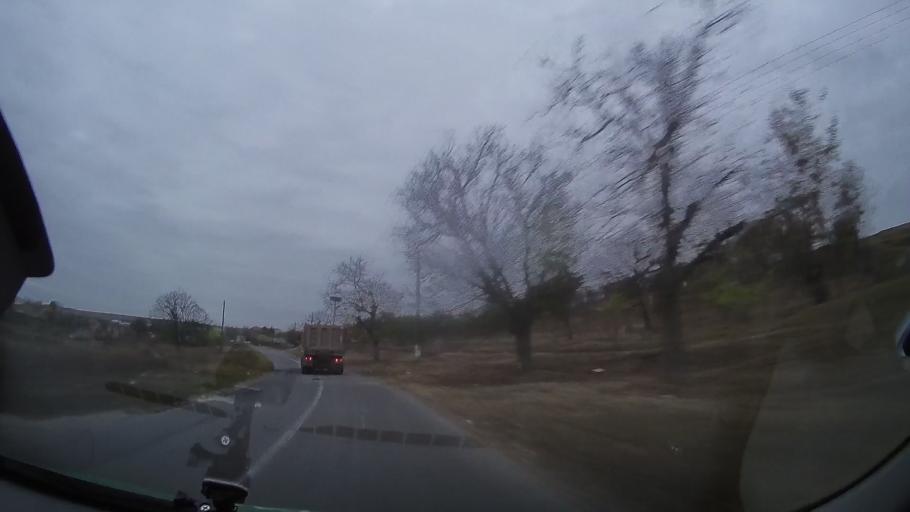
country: RO
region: Tulcea
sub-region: Comuna Mihai Bravu
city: Mihai Bravu
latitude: 44.9570
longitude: 28.6499
